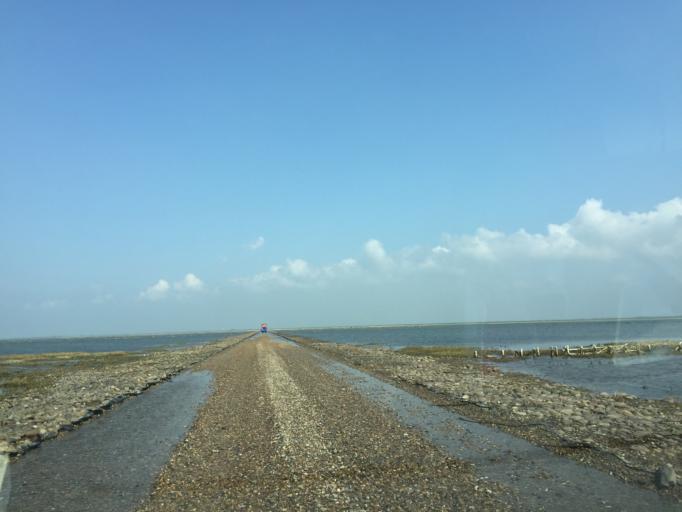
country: DK
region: South Denmark
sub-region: Esbjerg Kommune
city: Ribe
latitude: 55.3050
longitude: 8.6277
